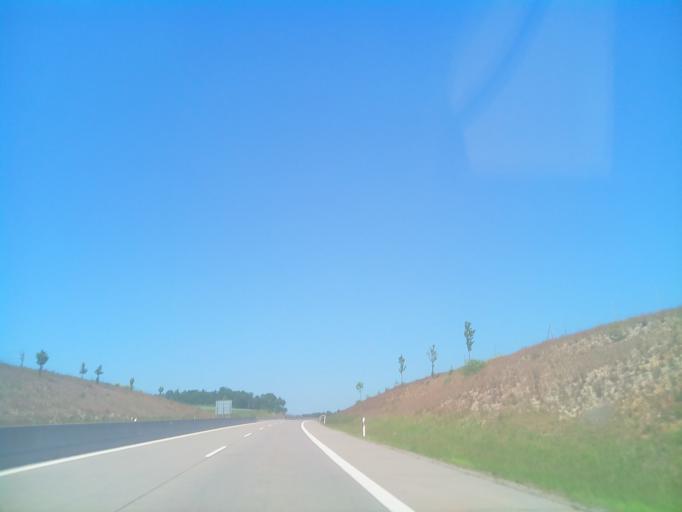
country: DE
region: Bavaria
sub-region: Regierungsbezirk Unterfranken
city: Munnerstadt
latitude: 50.2621
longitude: 10.2200
